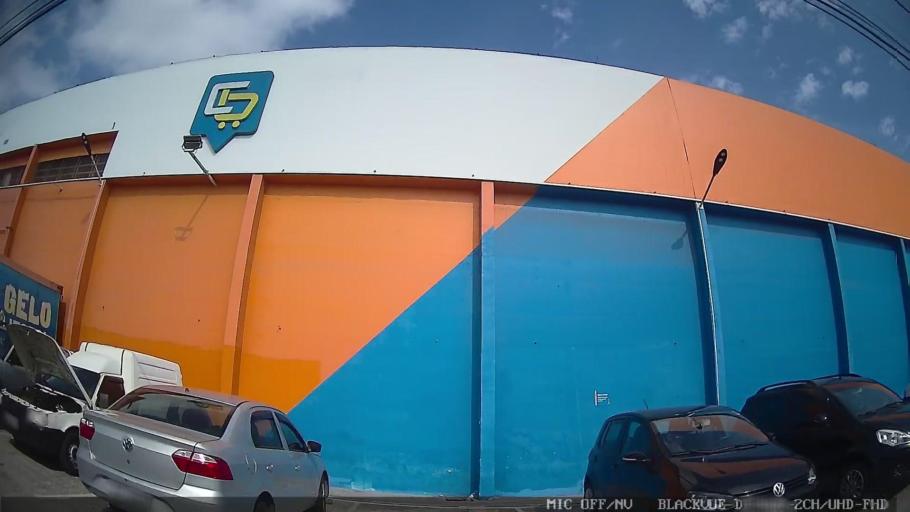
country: BR
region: Sao Paulo
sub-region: Santos
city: Santos
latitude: -23.9551
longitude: -46.2899
